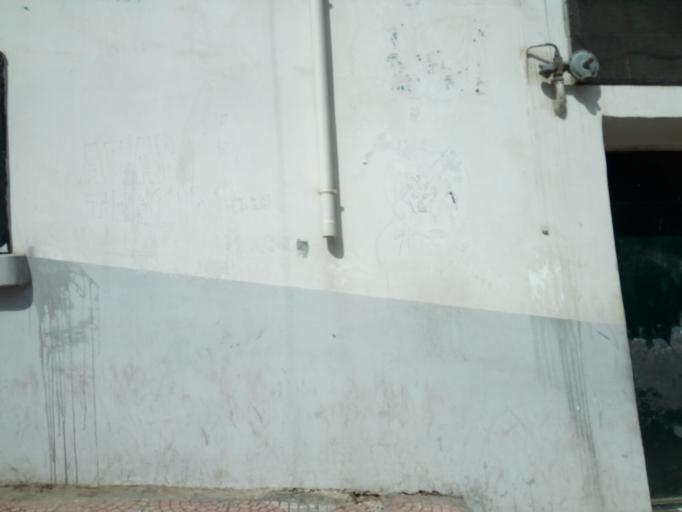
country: DZ
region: Constantine
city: Constantine
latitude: 36.3563
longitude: 6.6098
